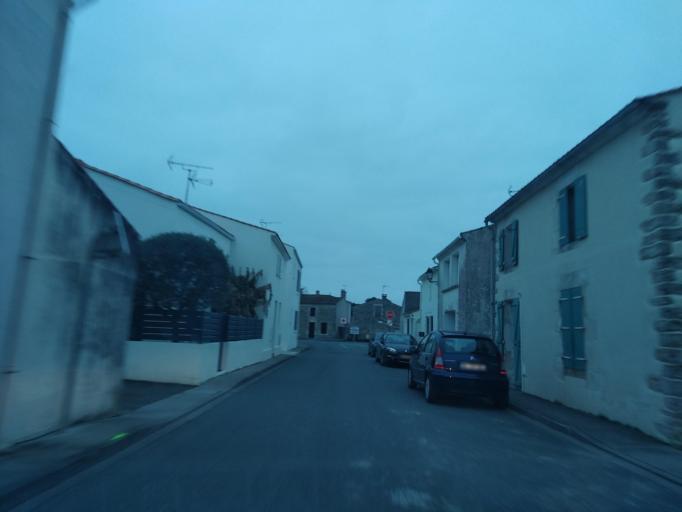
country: FR
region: Pays de la Loire
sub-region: Departement de la Vendee
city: Triaize
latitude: 46.3567
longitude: -1.2491
